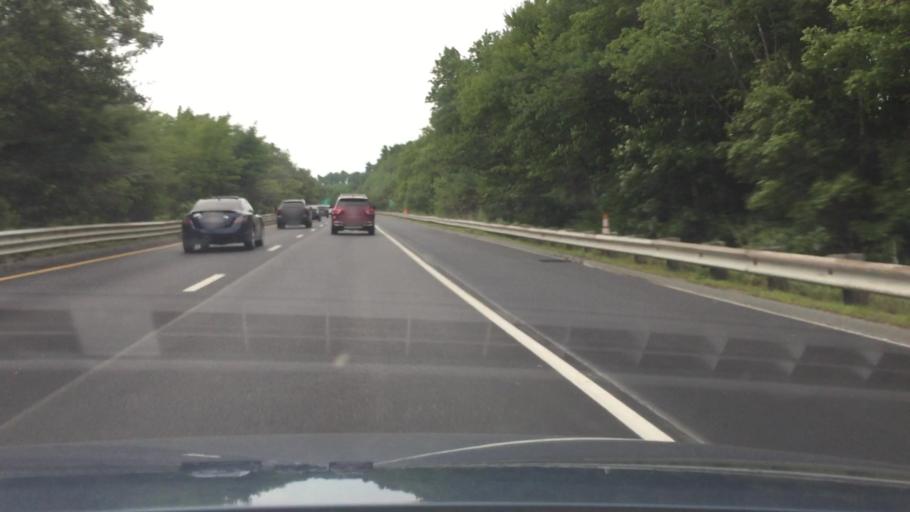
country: US
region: Massachusetts
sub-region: Plymouth County
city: South Duxbury
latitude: 42.0409
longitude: -70.7233
